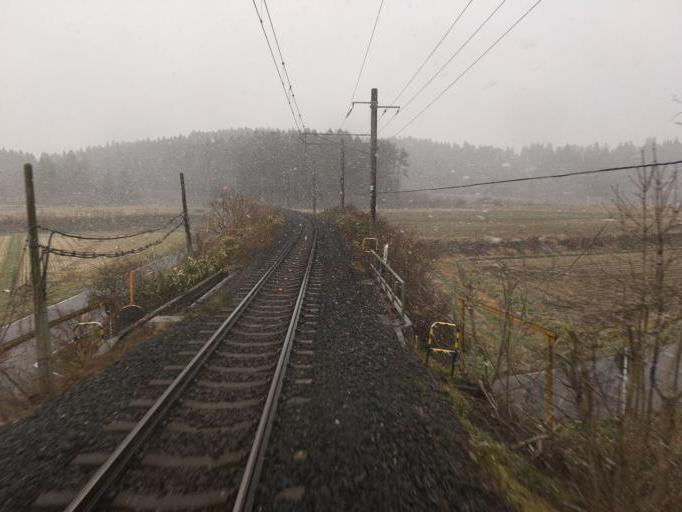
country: JP
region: Aomori
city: Aomori Shi
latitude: 41.0170
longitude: 140.6456
